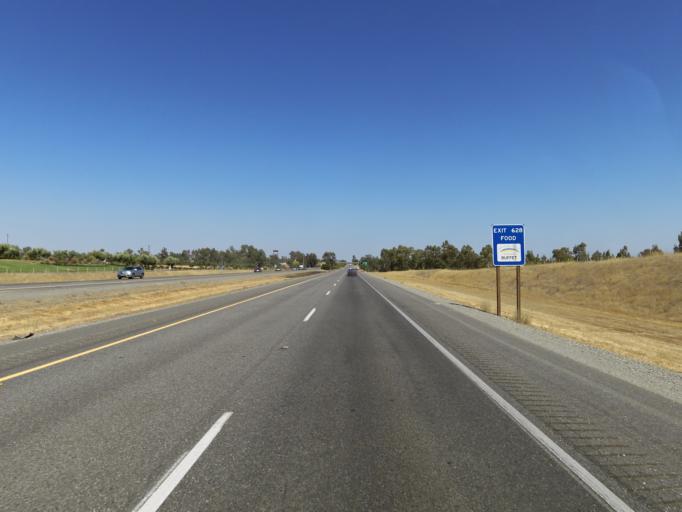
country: US
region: California
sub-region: Tehama County
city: Corning
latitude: 39.8741
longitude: -122.1999
